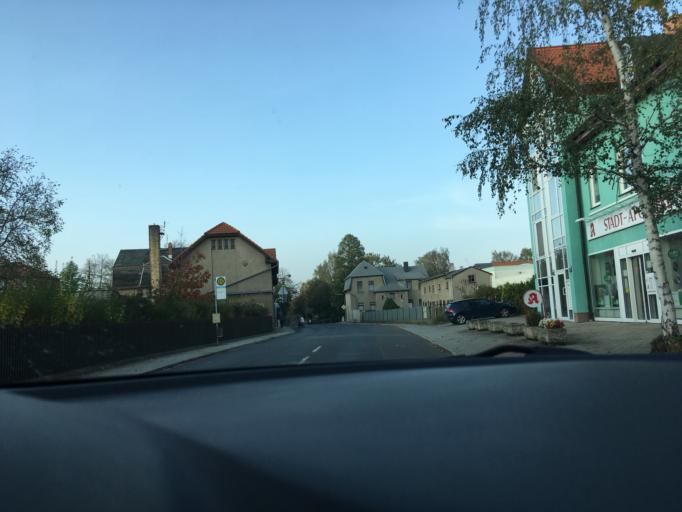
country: DE
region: Saxony
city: Rotha
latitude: 51.1993
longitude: 12.4167
